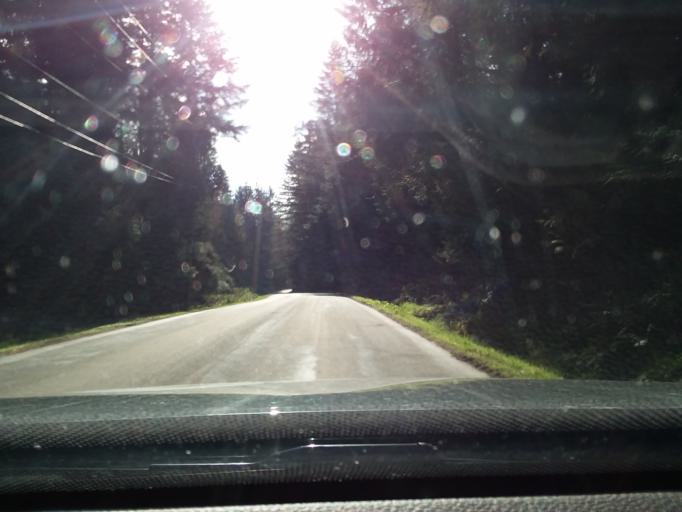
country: CA
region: British Columbia
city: North Cowichan
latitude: 48.9230
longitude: -123.4449
